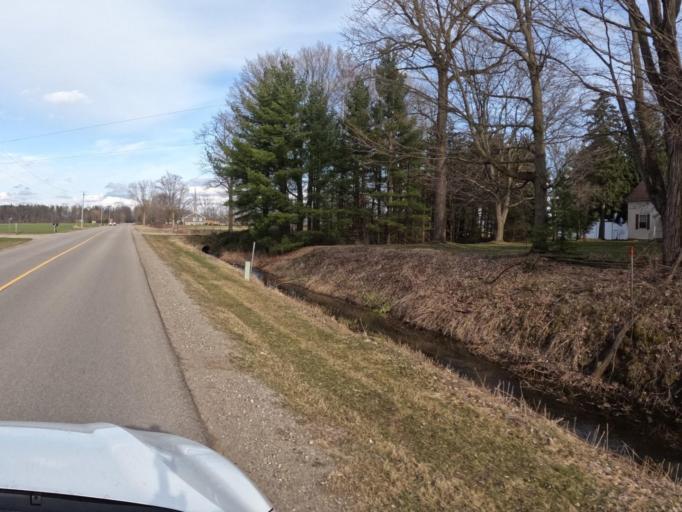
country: CA
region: Ontario
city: Brant
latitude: 43.0009
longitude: -80.4415
